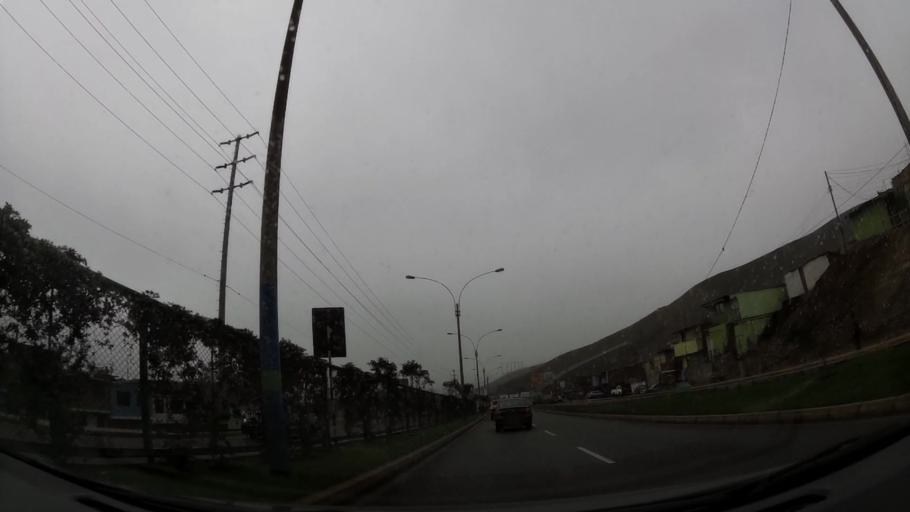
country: PE
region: Lima
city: Ventanilla
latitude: -11.8919
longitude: -77.1262
